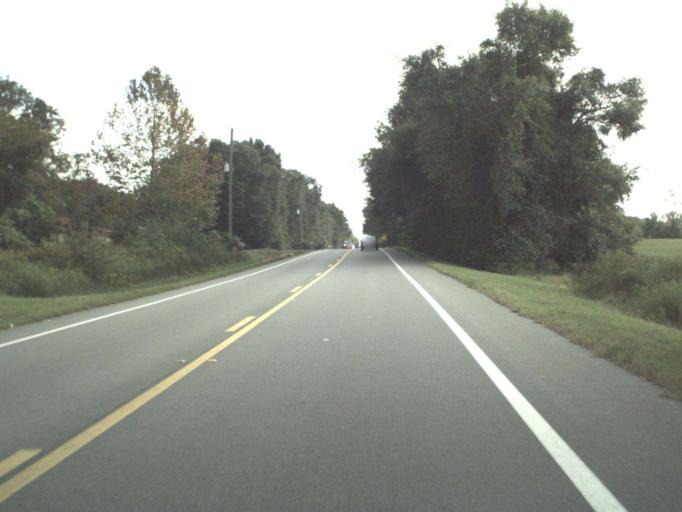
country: US
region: Florida
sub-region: Jackson County
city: Marianna
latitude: 30.6430
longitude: -85.1590
